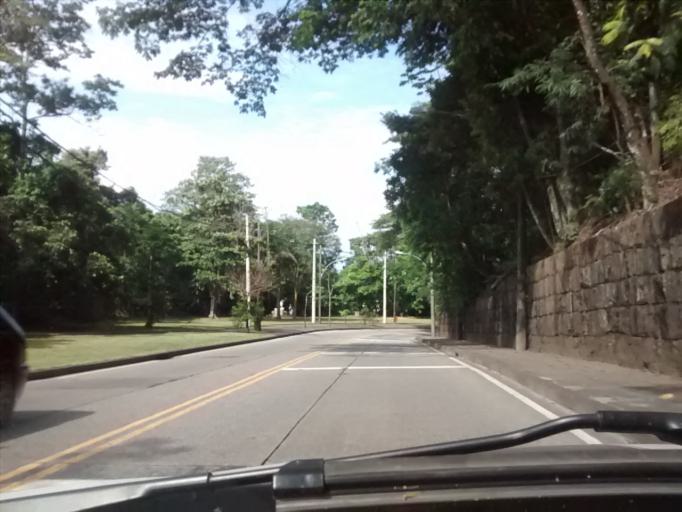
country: BR
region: Rio de Janeiro
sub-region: Rio De Janeiro
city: Rio de Janeiro
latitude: -22.9582
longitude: -43.2669
